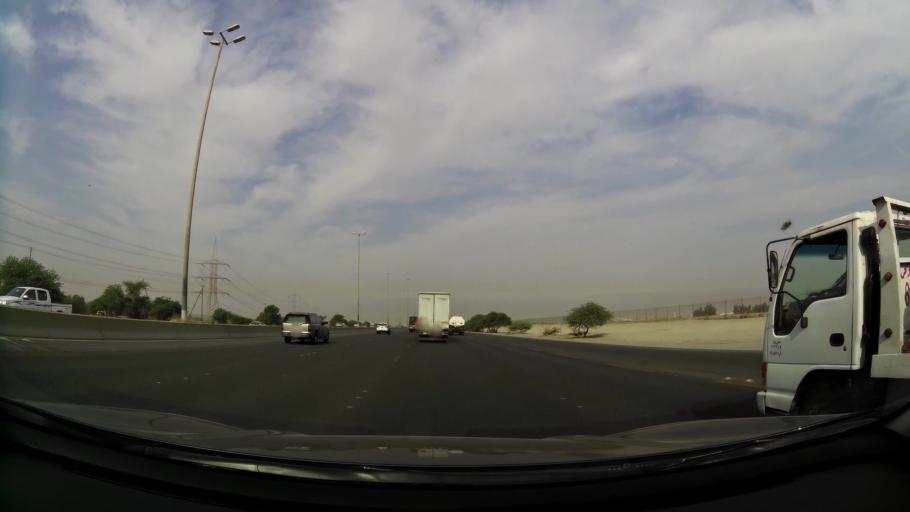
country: KW
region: Al Asimah
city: Ar Rabiyah
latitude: 29.2757
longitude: 47.8073
